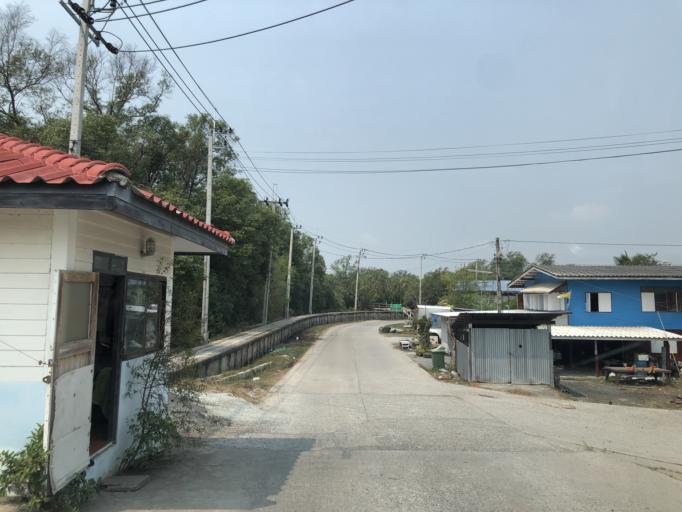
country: TH
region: Samut Prakan
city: Bang Bo
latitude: 13.5181
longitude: 100.8189
